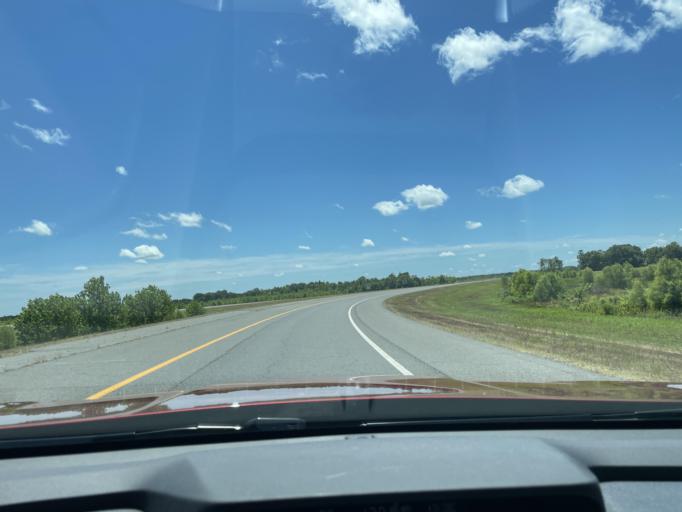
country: US
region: Arkansas
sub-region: Jefferson County
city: Pine Bluff
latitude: 34.1723
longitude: -91.9869
